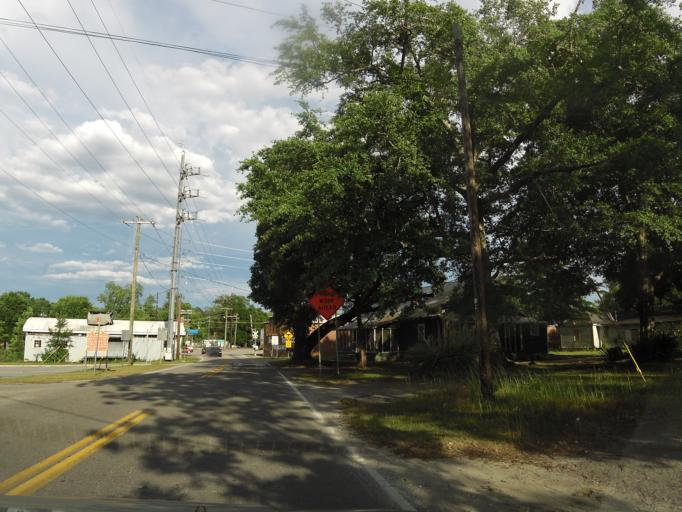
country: US
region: South Carolina
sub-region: Hampton County
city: Estill
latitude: 32.7579
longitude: -81.2425
